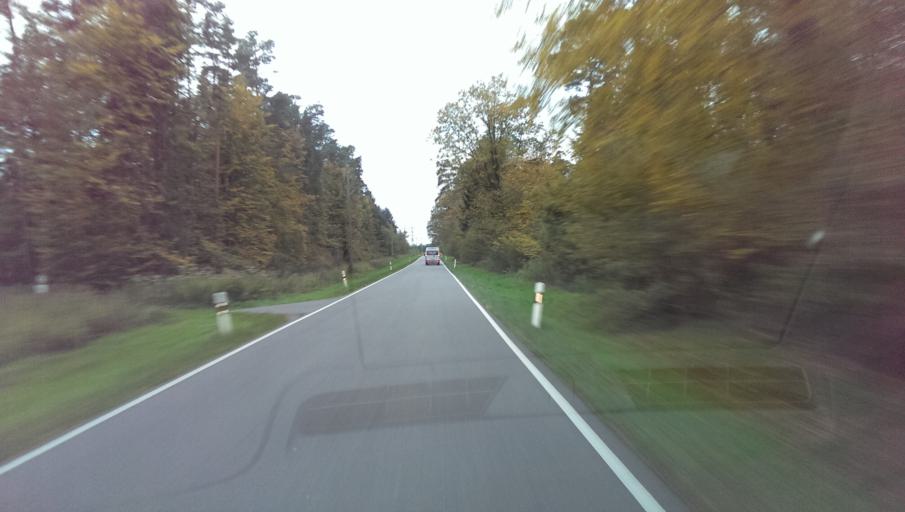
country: DE
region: Rheinland-Pfalz
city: Hagenbach
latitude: 49.0253
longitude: 8.2045
